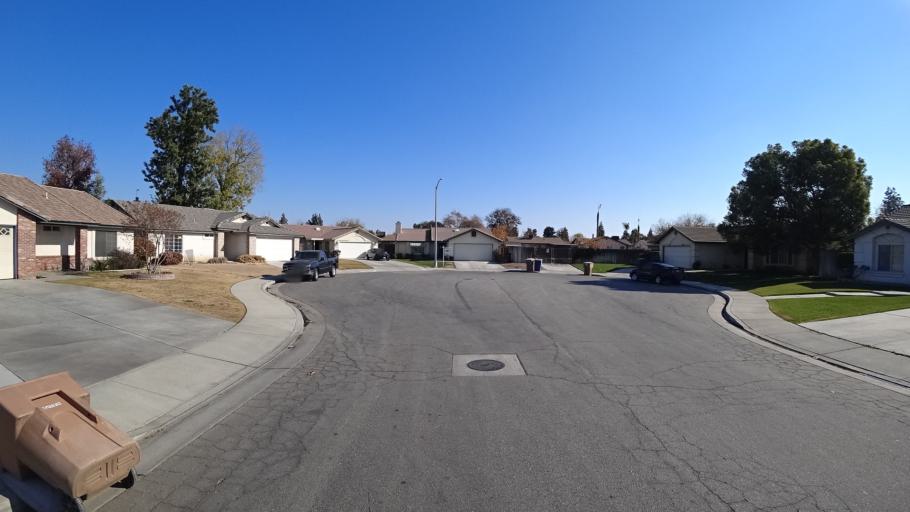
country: US
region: California
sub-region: Kern County
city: Greenfield
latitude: 35.3007
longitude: -119.0555
